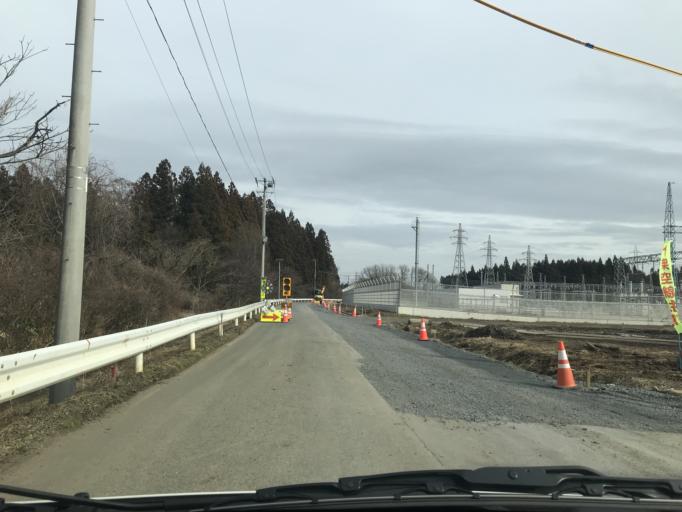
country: JP
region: Iwate
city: Hanamaki
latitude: 39.3368
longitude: 141.0677
